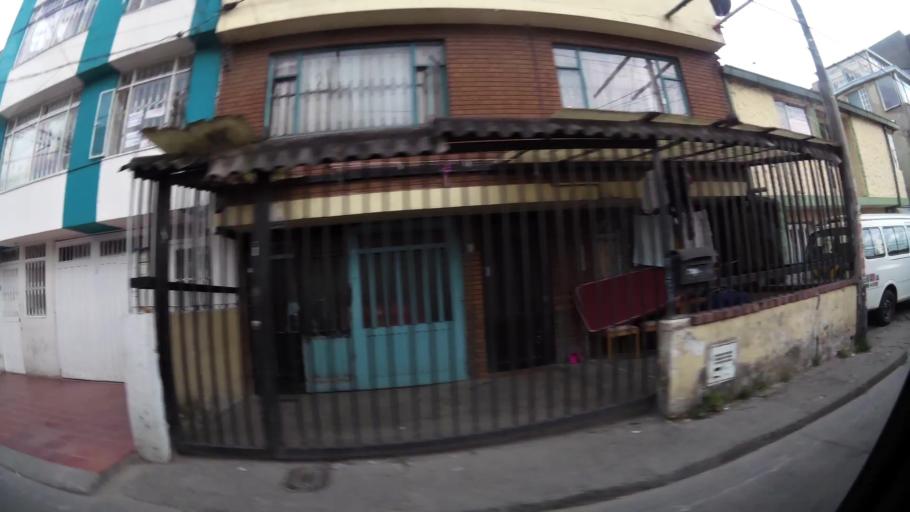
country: CO
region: Cundinamarca
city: La Calera
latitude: 4.7384
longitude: -74.0259
